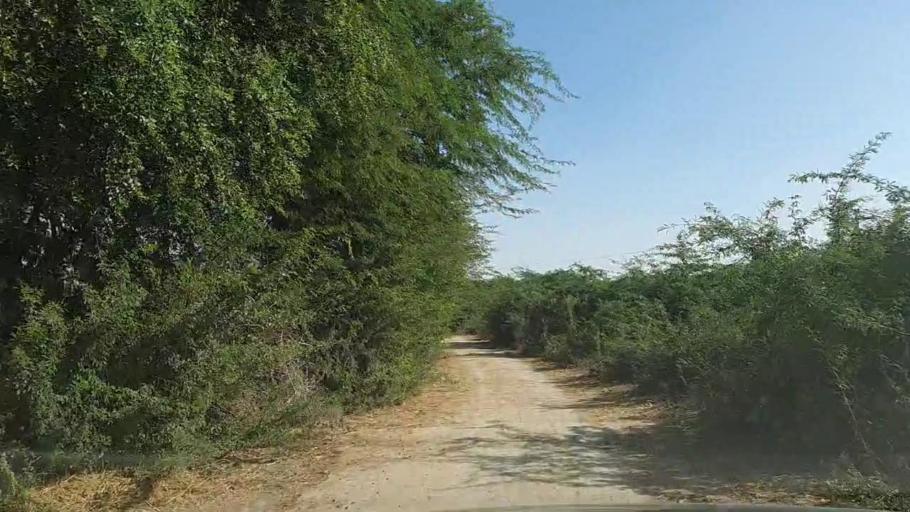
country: PK
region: Sindh
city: Daro Mehar
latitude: 24.7722
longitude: 68.0671
